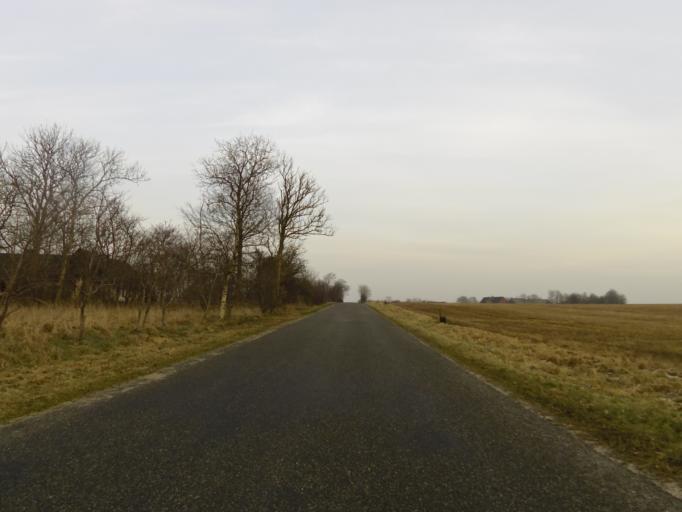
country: DK
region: South Denmark
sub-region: Esbjerg Kommune
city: Ribe
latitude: 55.3471
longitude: 8.9134
